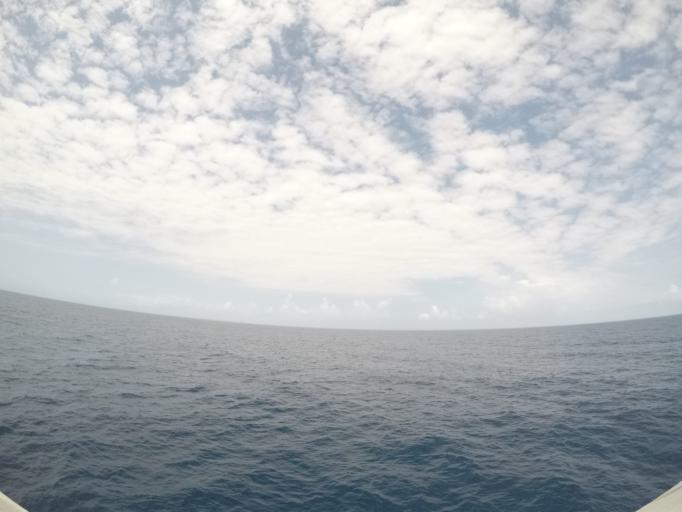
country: TZ
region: Zanzibar North
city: Nungwi
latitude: -5.5938
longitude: 39.3468
